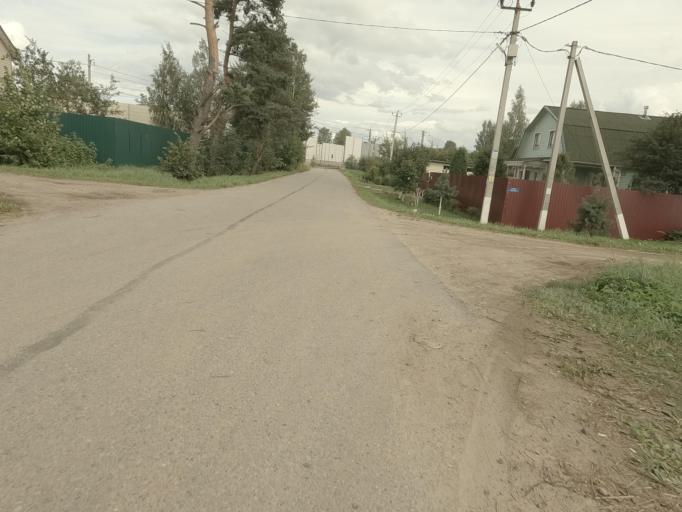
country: RU
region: Leningrad
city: Mga
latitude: 59.7597
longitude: 31.0363
